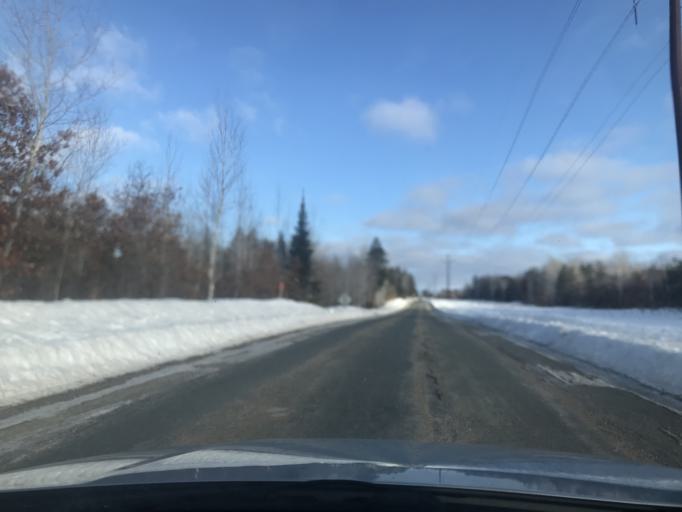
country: US
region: Wisconsin
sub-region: Marinette County
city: Niagara
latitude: 45.5926
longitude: -87.9769
